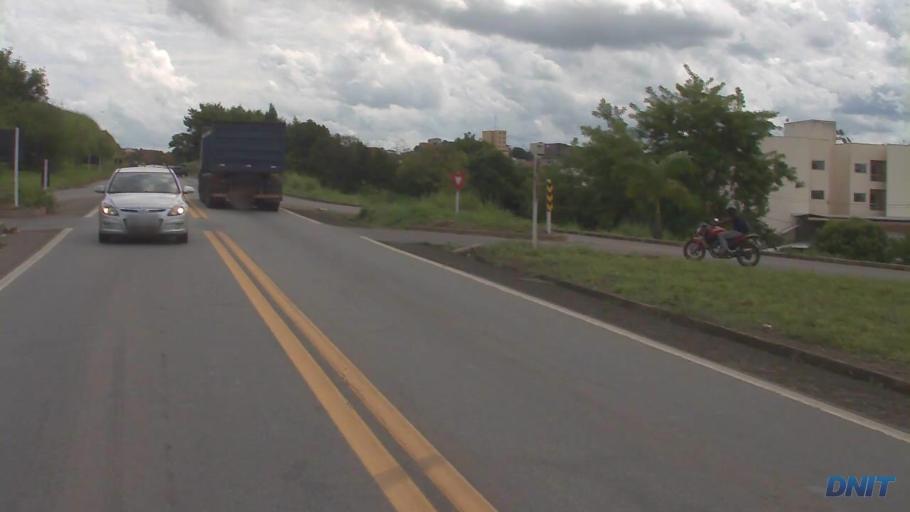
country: BR
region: Minas Gerais
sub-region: Ipatinga
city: Ipatinga
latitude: -19.4554
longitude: -42.5230
